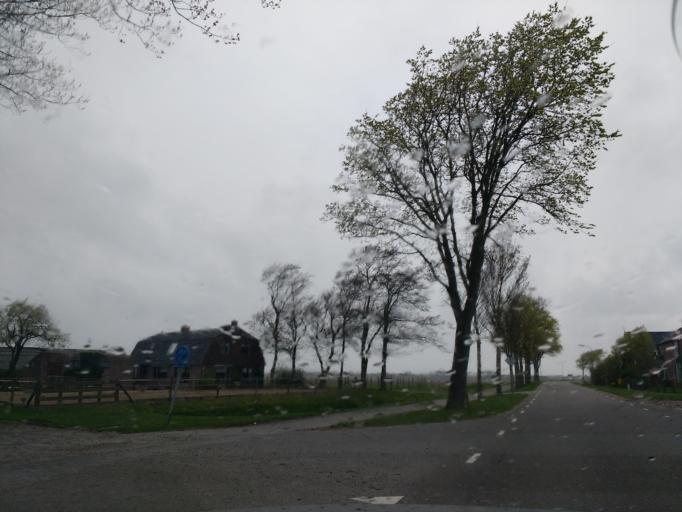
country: NL
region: North Holland
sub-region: Gemeente Schagen
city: Harenkarspel
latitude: 52.7534
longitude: 4.7473
